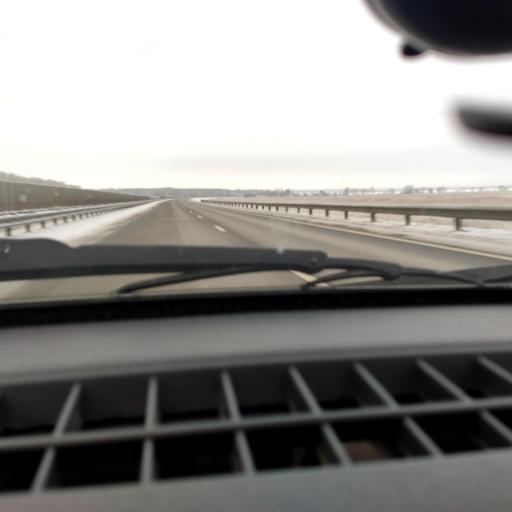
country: RU
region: Bashkortostan
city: Kushnarenkovo
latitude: 55.0605
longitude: 55.3916
